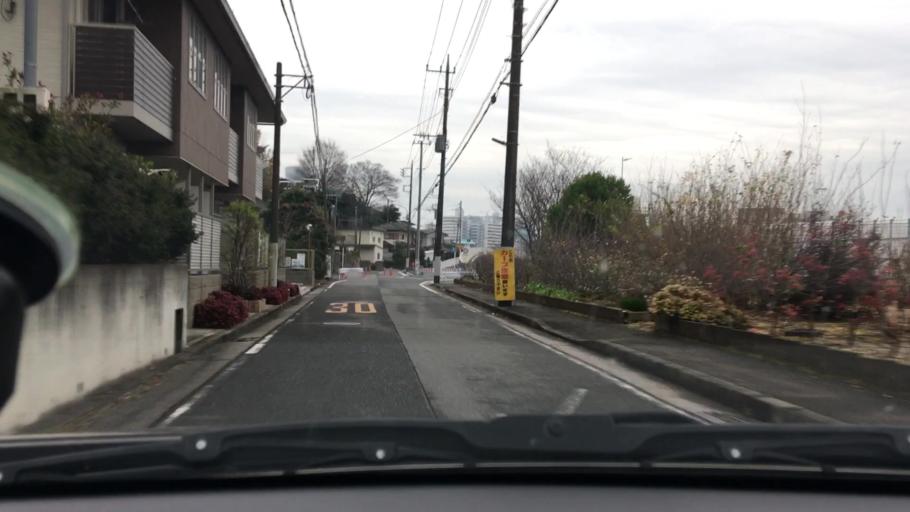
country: JP
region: Kanagawa
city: Yokohama
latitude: 35.5172
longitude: 139.6062
